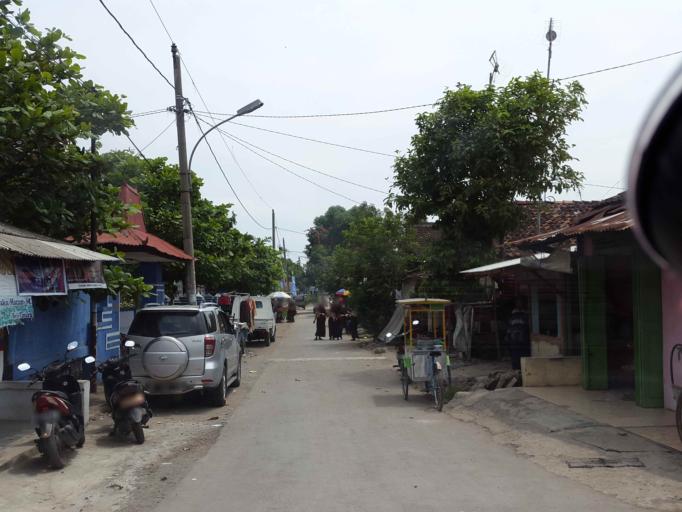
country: ID
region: Central Java
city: Petarukan
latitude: -6.8931
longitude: 109.4099
